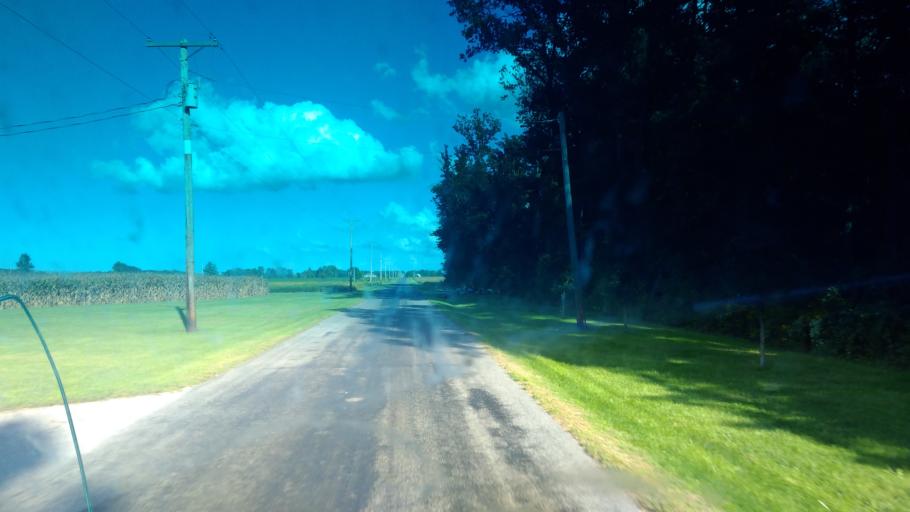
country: US
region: Ohio
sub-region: Hancock County
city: Arlington
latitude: 40.9362
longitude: -83.7117
